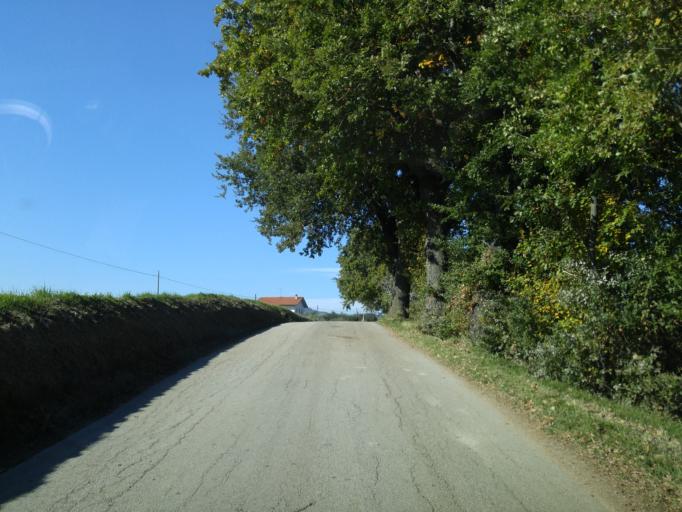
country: IT
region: The Marches
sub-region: Provincia di Pesaro e Urbino
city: Serrungarina
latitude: 43.7387
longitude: 12.8768
